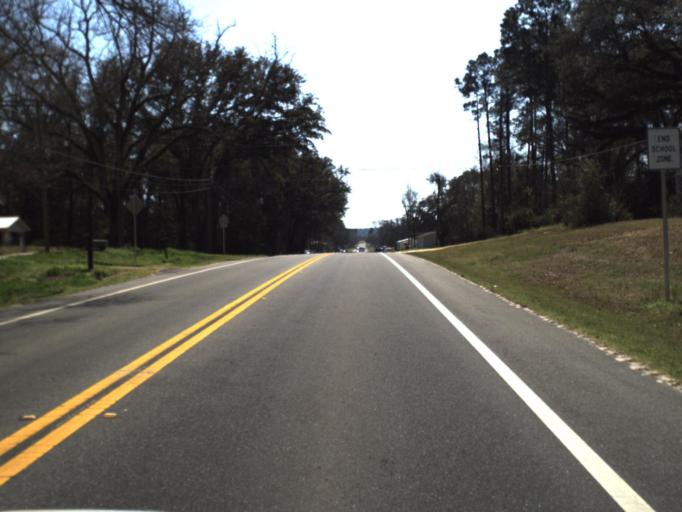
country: US
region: Florida
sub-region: Jackson County
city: Sneads
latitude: 30.7078
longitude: -85.0203
